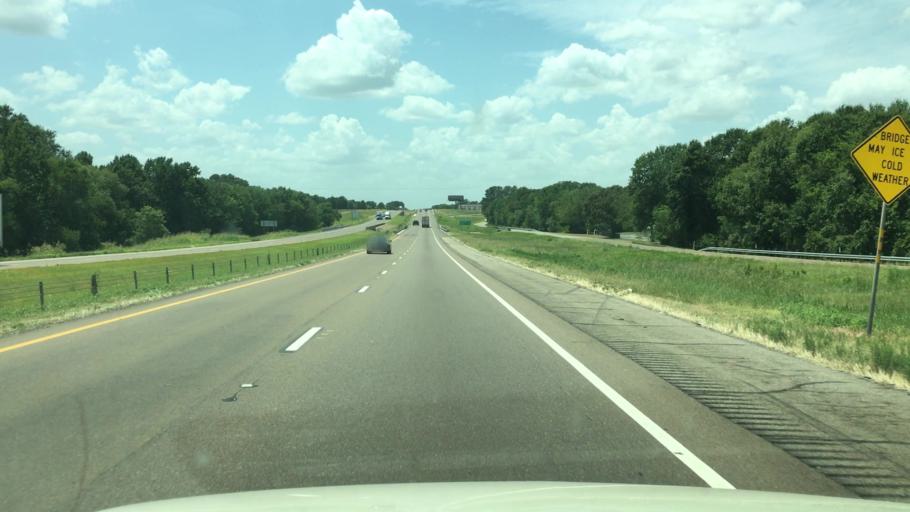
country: US
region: Texas
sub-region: Titus County
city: Mount Pleasant
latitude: 33.1660
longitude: -95.0123
